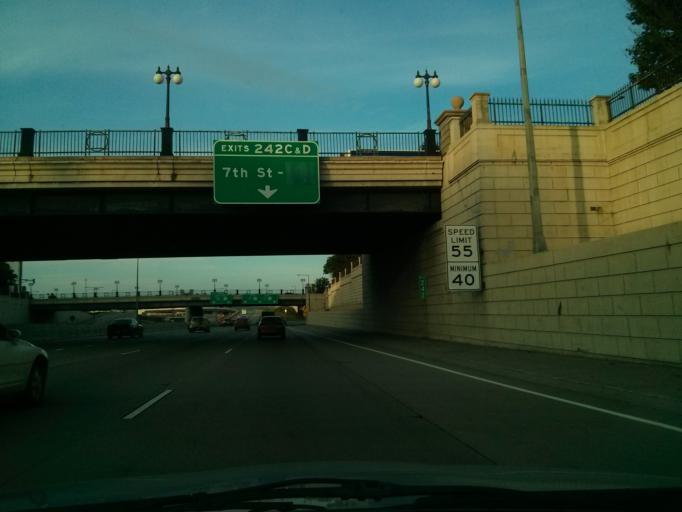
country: US
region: Minnesota
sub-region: Ramsey County
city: Saint Paul
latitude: 44.9522
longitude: -93.0962
